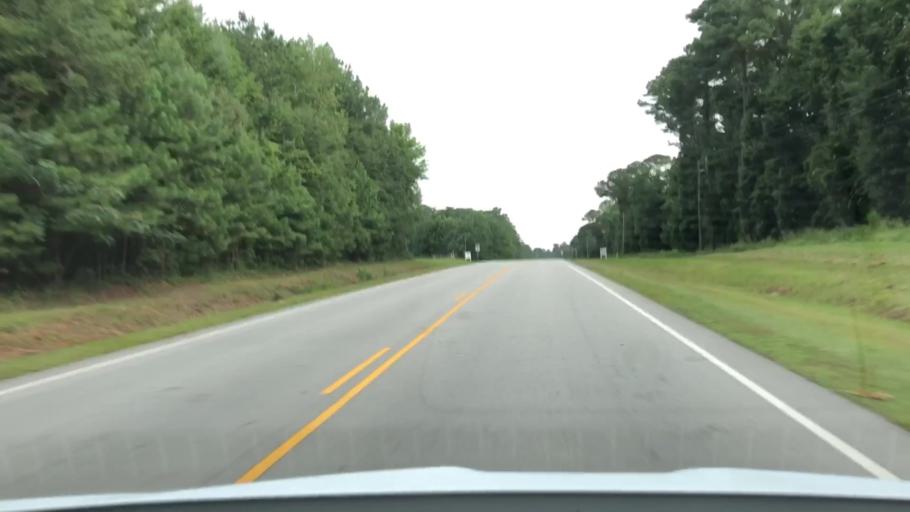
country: US
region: North Carolina
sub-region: Jones County
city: Trenton
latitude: 35.0106
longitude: -77.2882
